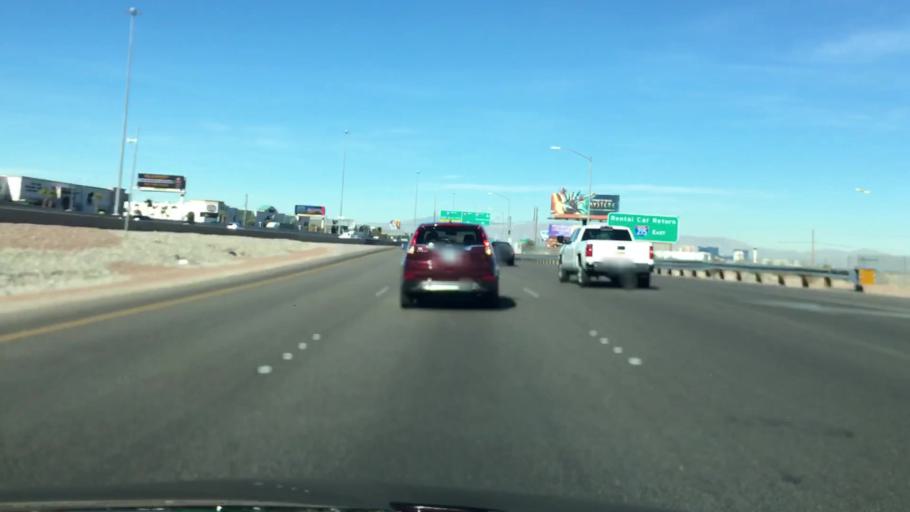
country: US
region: Nevada
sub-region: Clark County
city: Paradise
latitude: 36.0470
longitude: -115.1801
